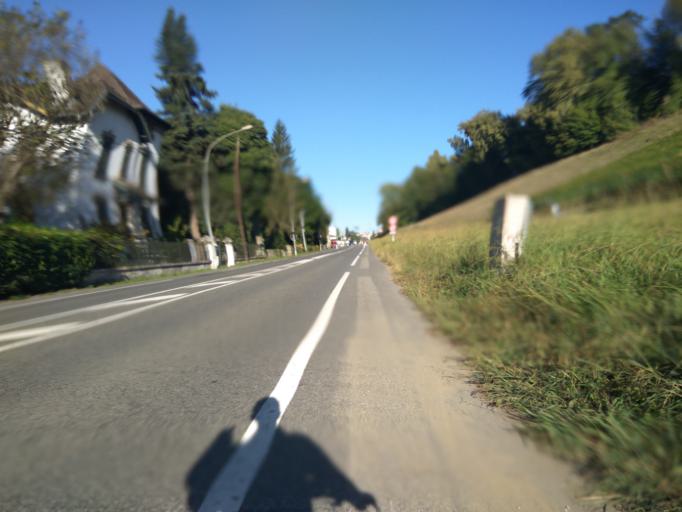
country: FR
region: Aquitaine
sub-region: Departement des Pyrenees-Atlantiques
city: Bizanos
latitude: 43.2851
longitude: -0.3471
